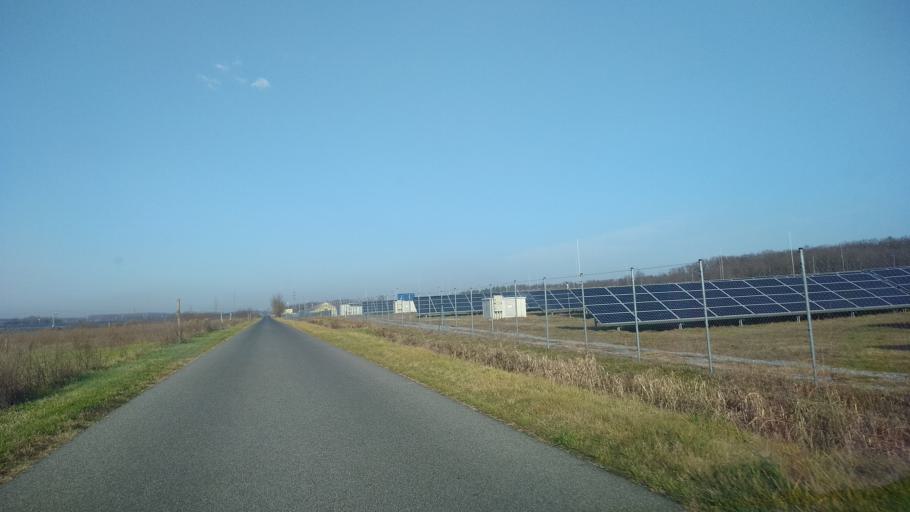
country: HU
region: Somogy
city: Barcs
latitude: 45.9676
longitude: 17.4977
